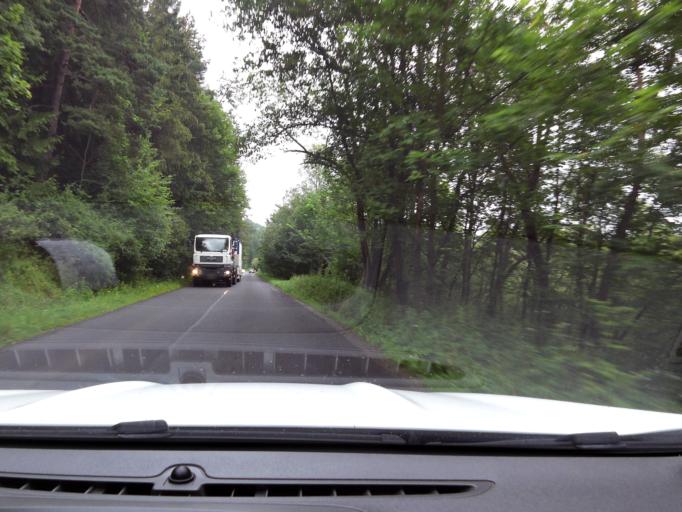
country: PL
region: Silesian Voivodeship
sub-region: Powiat zywiecki
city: Rajcza
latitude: 49.4929
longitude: 19.1144
